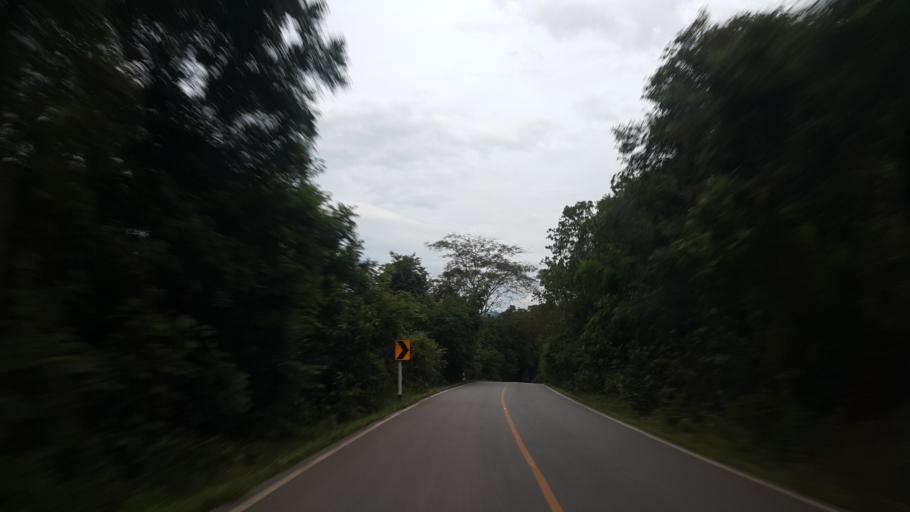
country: TH
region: Loei
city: Na Haeo
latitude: 17.5303
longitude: 101.1993
